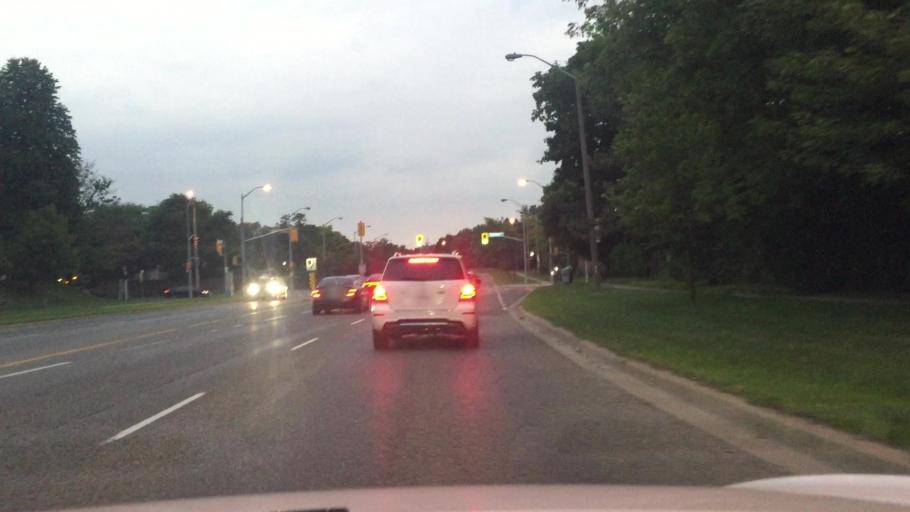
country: CA
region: Ontario
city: Willowdale
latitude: 43.7931
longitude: -79.3360
